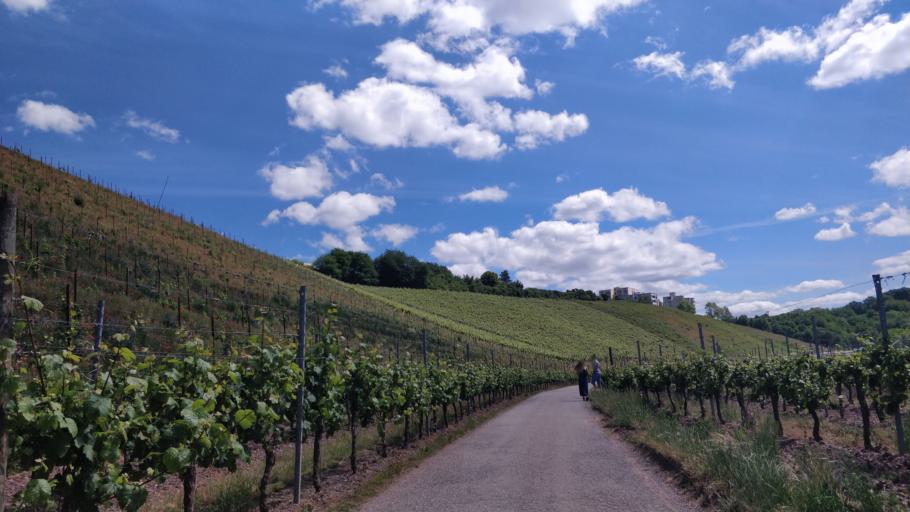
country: DE
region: Rheinland-Pfalz
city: Trier
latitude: 49.7385
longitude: 6.6612
